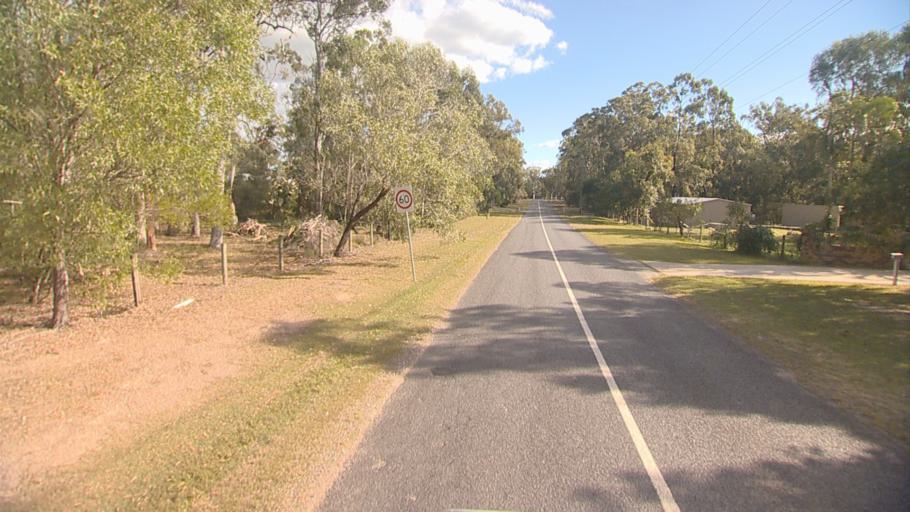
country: AU
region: Queensland
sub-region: Gold Coast
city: Yatala
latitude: -27.6575
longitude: 153.2445
